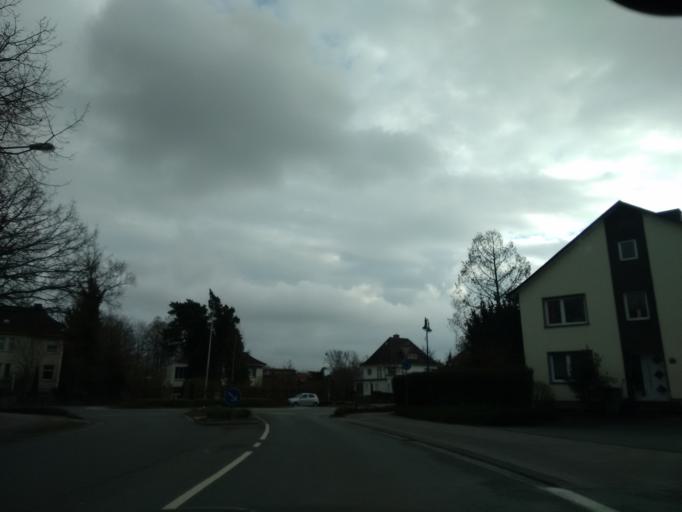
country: DE
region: North Rhine-Westphalia
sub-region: Regierungsbezirk Detmold
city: Salzkotten
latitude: 51.6717
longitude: 8.6011
